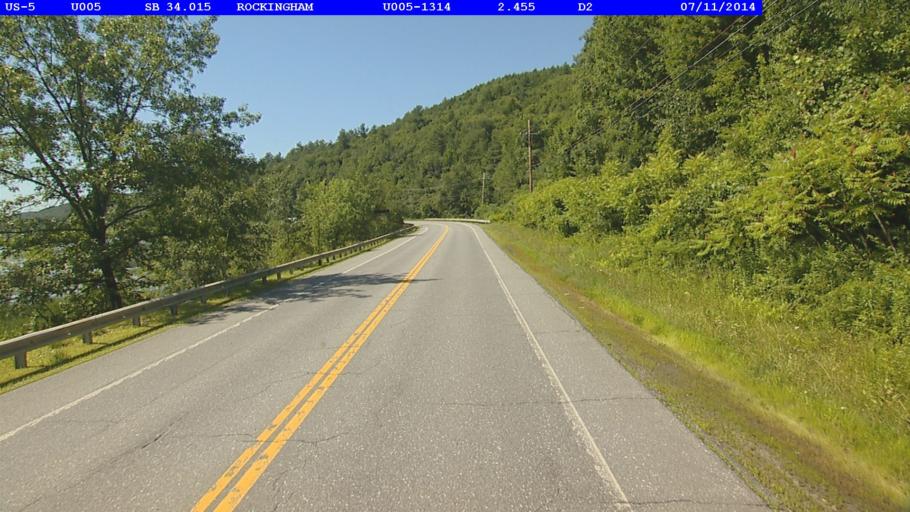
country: US
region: Vermont
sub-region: Windham County
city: Bellows Falls
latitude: 43.1565
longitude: -72.4585
